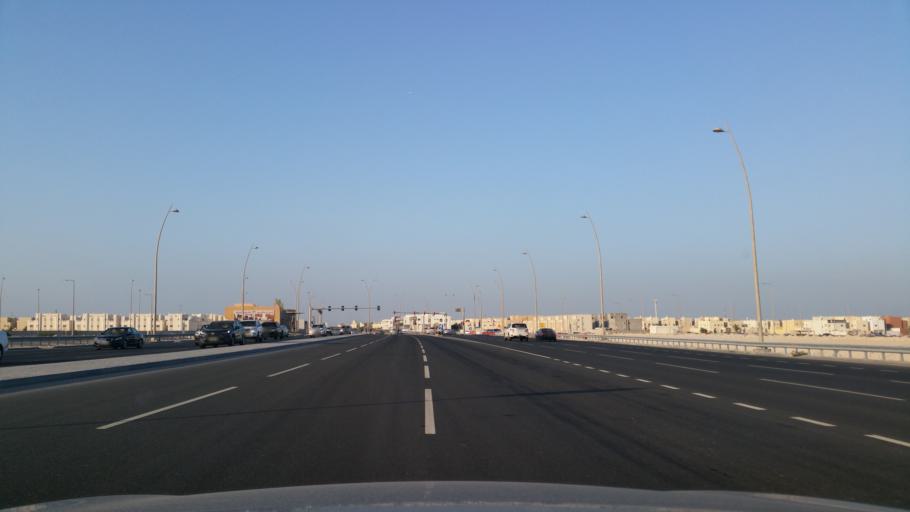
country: QA
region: Al Khawr
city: Al Khawr
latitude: 25.6616
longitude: 51.5006
